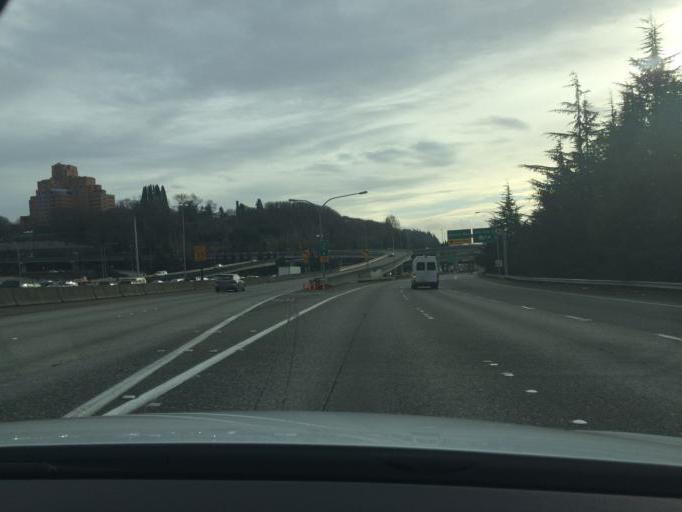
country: US
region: Washington
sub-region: King County
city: Seattle
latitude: 47.5974
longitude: -122.3211
